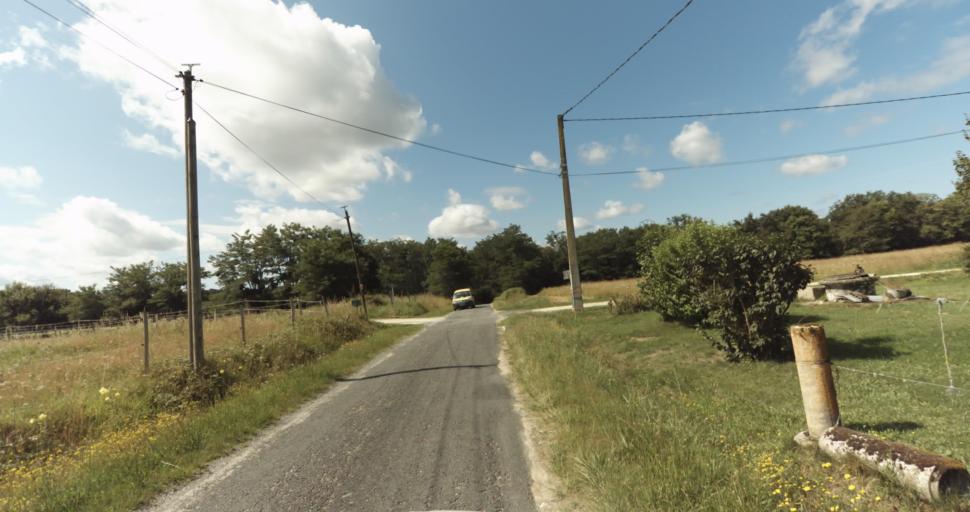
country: FR
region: Aquitaine
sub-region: Departement de la Gironde
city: Bazas
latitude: 44.4662
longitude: -0.2174
